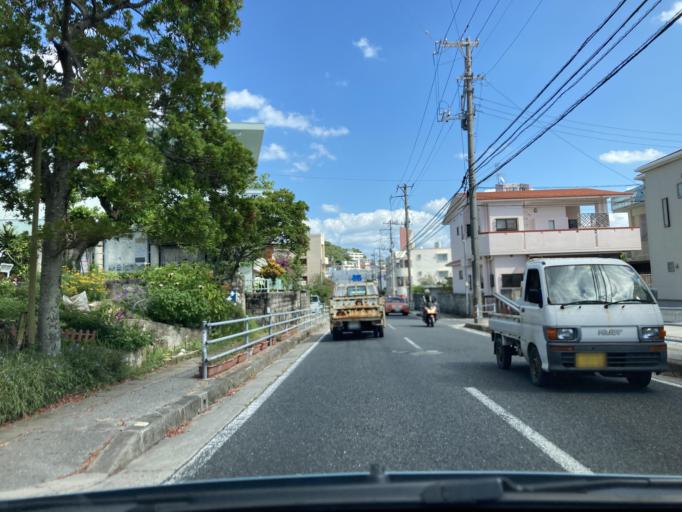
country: JP
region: Okinawa
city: Tomigusuku
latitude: 26.1857
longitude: 127.7248
